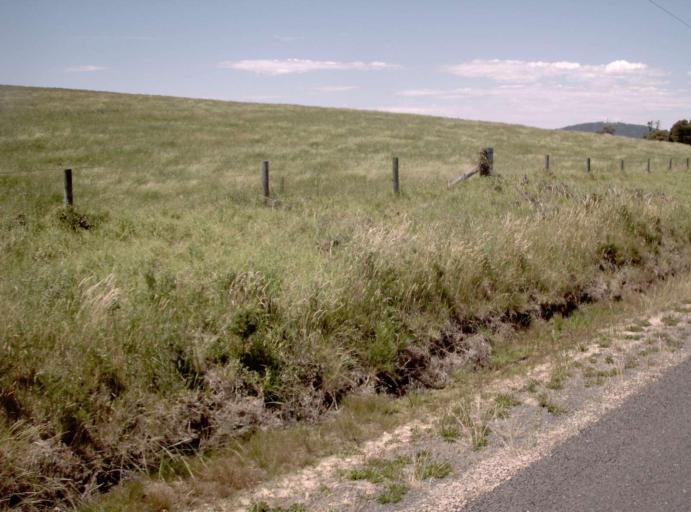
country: AU
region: Victoria
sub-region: East Gippsland
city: Lakes Entrance
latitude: -37.7049
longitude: 148.5229
